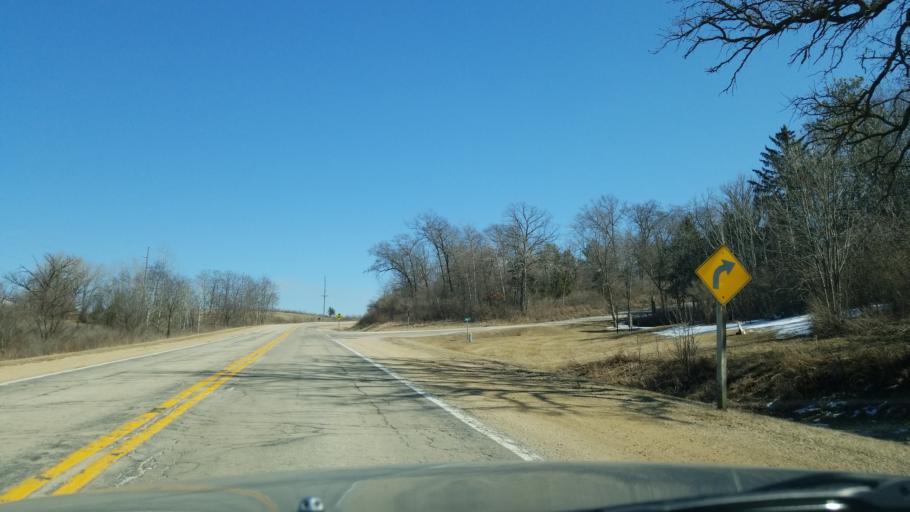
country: US
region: Wisconsin
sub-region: Iowa County
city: Mineral Point
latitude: 42.9131
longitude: -90.2625
